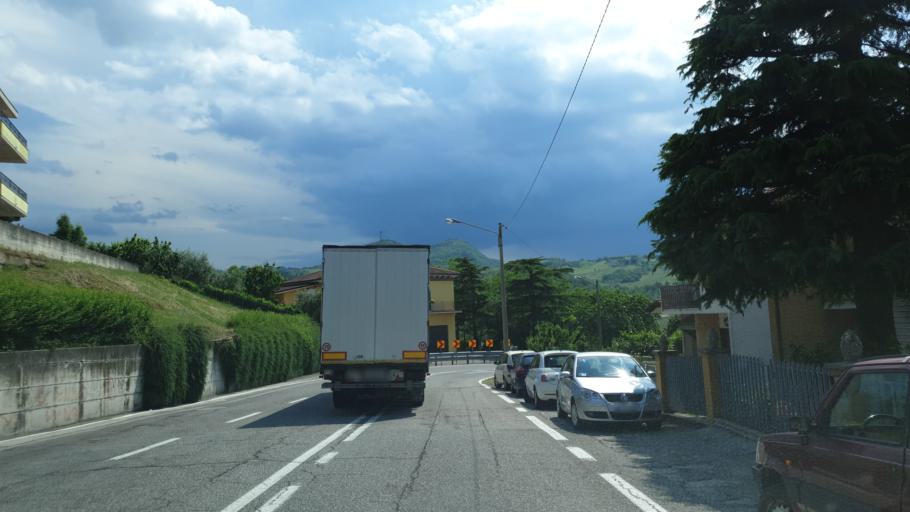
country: SM
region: Acquaviva
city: Acquaviva
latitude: 43.9484
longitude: 12.4085
